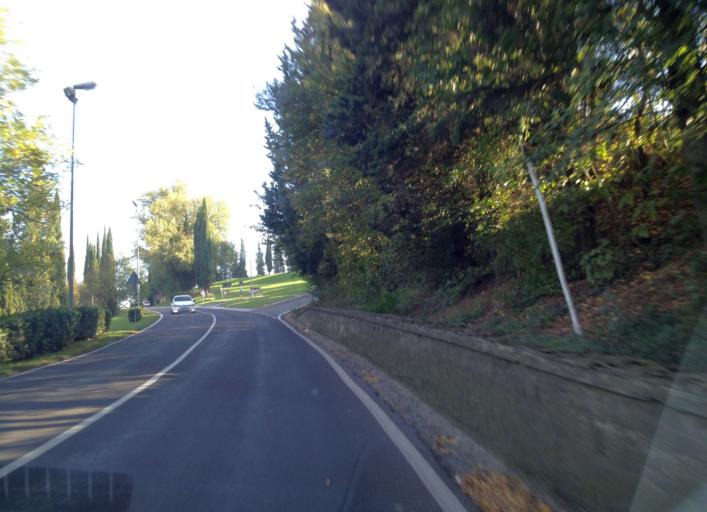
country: IT
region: Tuscany
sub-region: Provincia di Siena
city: Poggibonsi
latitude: 43.4597
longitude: 11.1475
